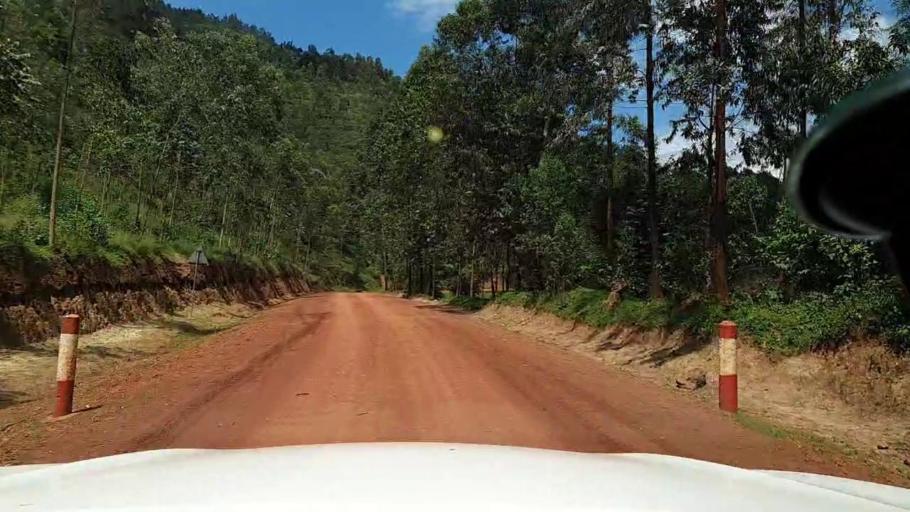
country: RW
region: Northern Province
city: Byumba
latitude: -1.7470
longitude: 29.8644
